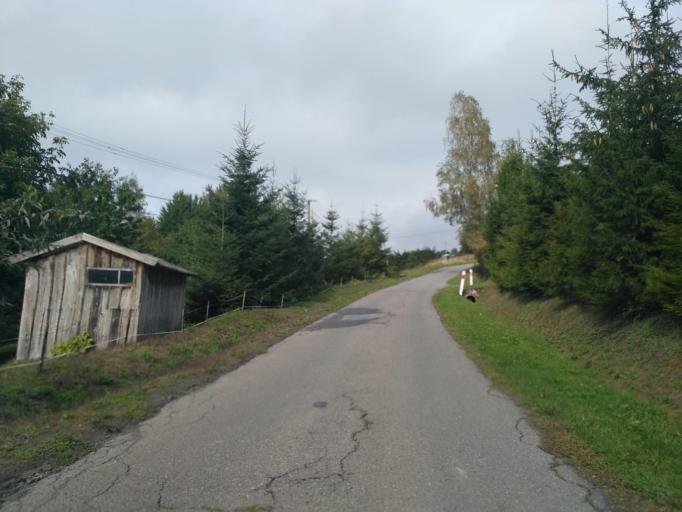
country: PL
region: Subcarpathian Voivodeship
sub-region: Powiat debicki
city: Brzostek
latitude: 49.9554
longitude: 21.4400
